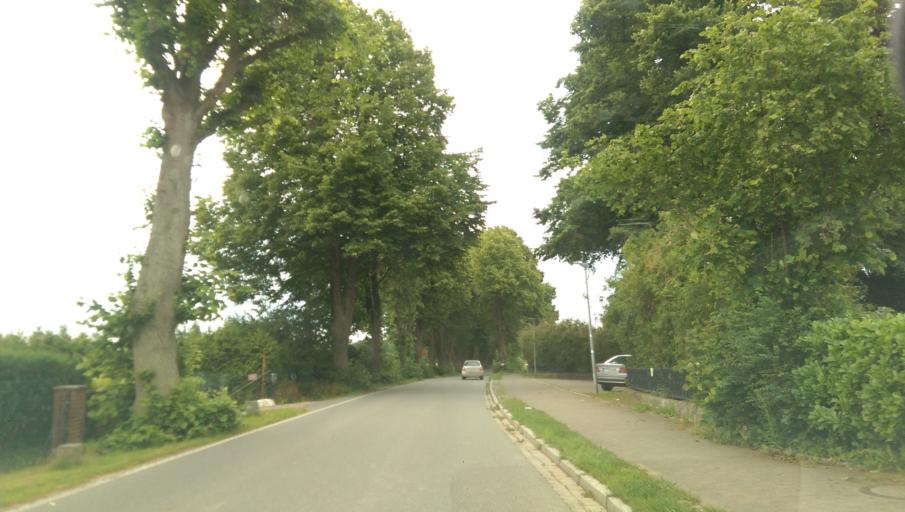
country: DE
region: Schleswig-Holstein
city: Travemuende
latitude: 53.9857
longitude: 10.8334
